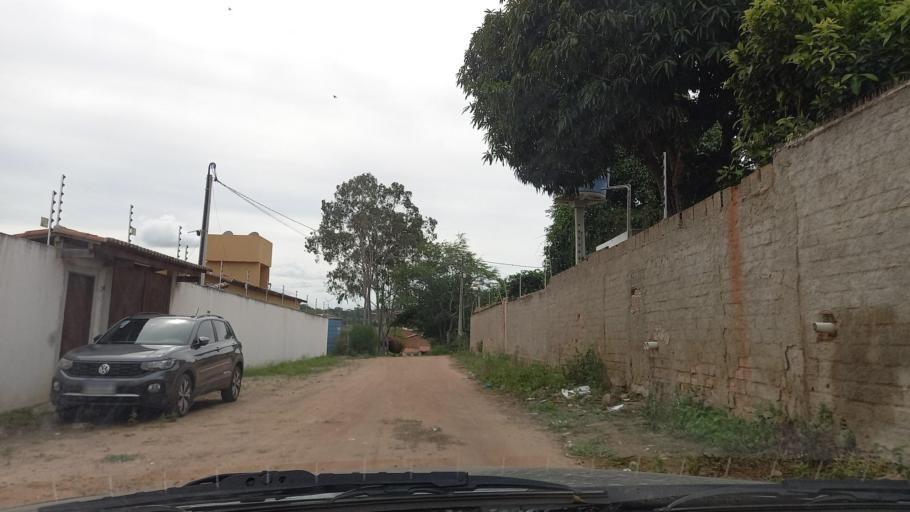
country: BR
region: Pernambuco
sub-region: Gravata
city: Gravata
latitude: -8.1957
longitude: -35.5958
